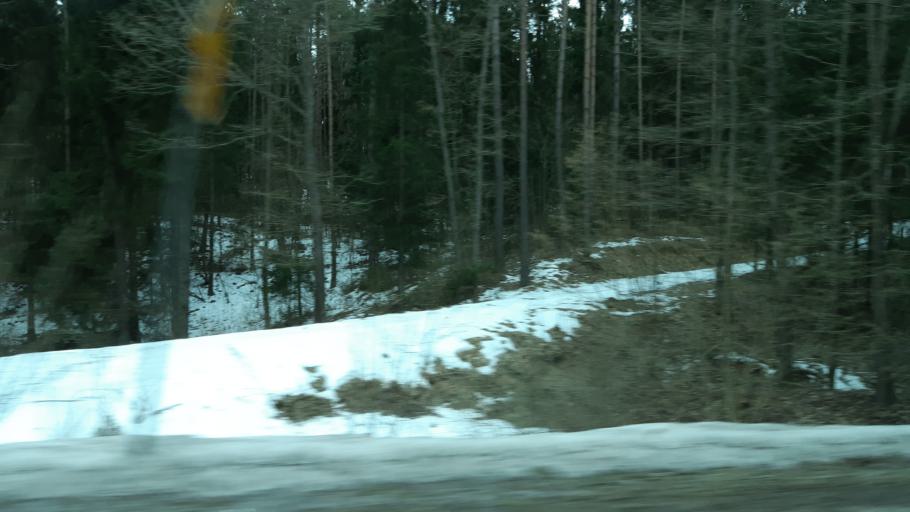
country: PL
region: Podlasie
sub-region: Suwalki
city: Suwalki
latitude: 54.2913
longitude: 22.9561
